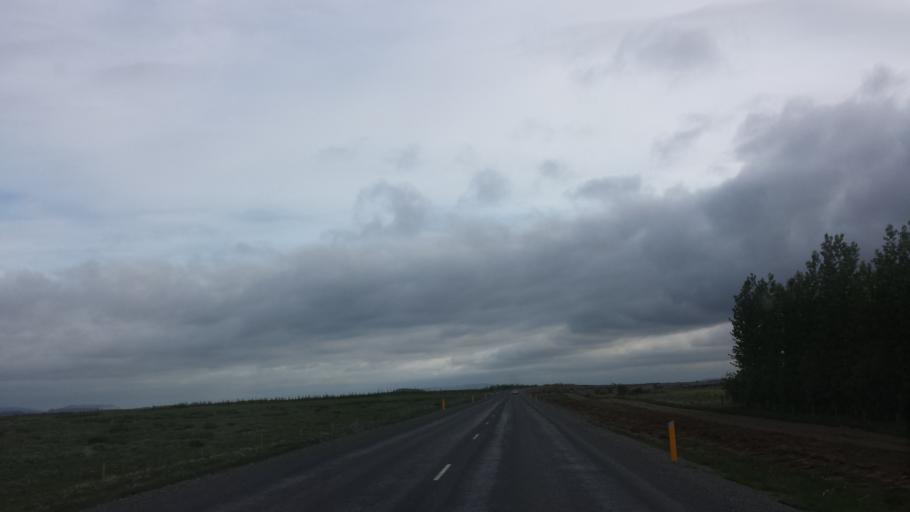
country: IS
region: South
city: Selfoss
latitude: 64.2811
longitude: -20.3450
